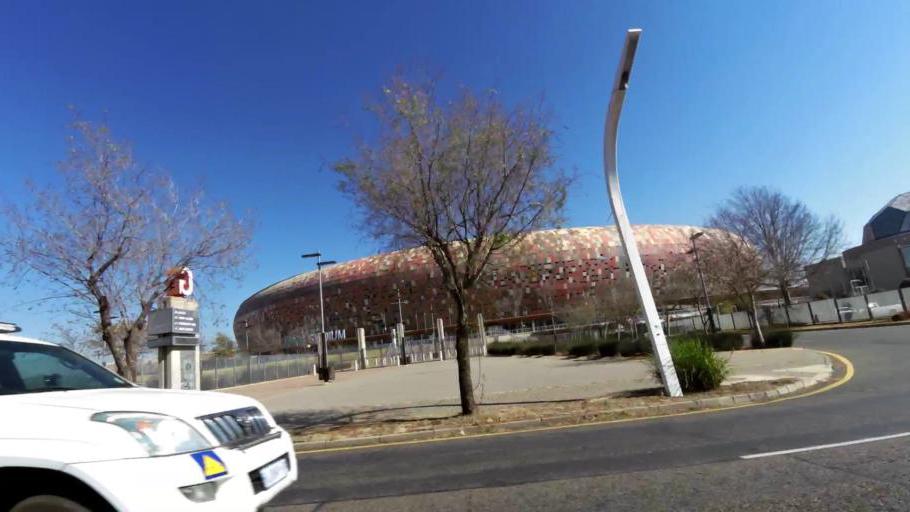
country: ZA
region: Gauteng
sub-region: City of Johannesburg Metropolitan Municipality
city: Johannesburg
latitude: -26.2352
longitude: 27.9855
